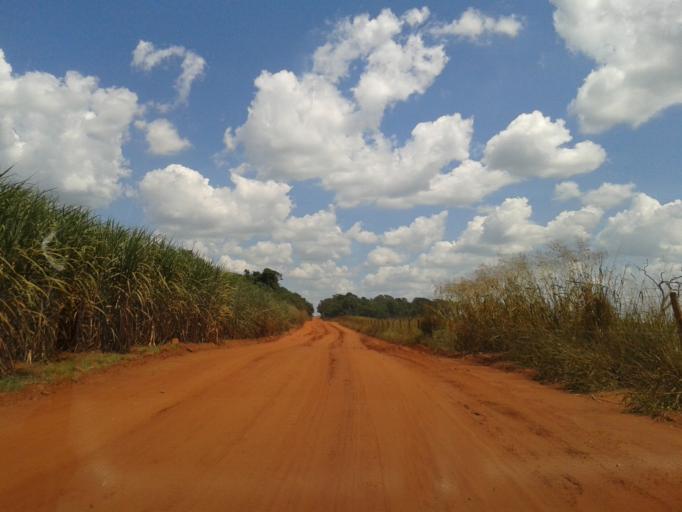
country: BR
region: Minas Gerais
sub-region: Ituiutaba
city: Ituiutaba
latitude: -19.0443
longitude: -49.7107
